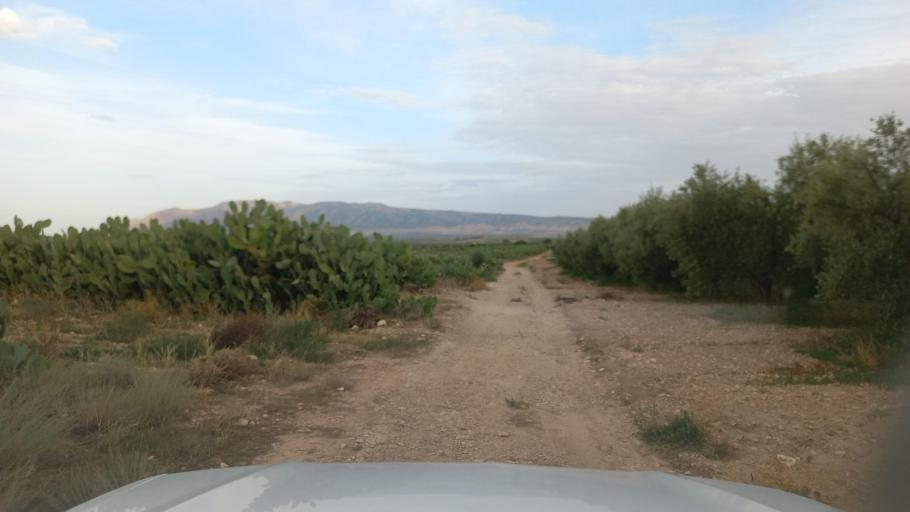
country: TN
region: Al Qasrayn
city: Sbiba
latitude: 35.4397
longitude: 9.0877
